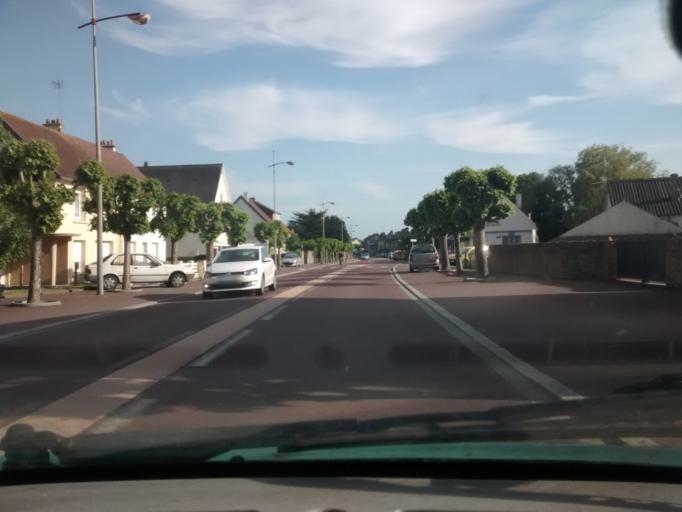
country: FR
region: Lower Normandy
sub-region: Departement de la Manche
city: Lessay
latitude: 49.2193
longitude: -1.5315
